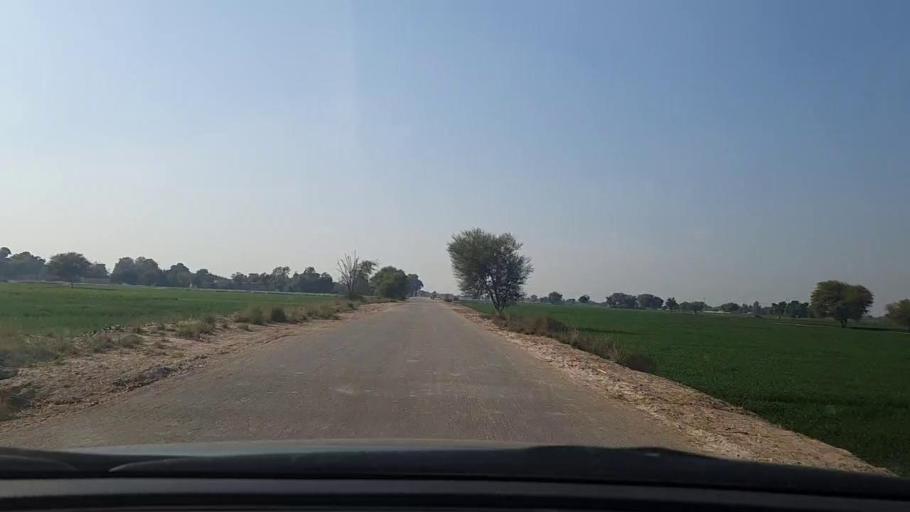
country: PK
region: Sindh
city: Daulatpur
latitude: 26.3169
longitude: 68.0602
